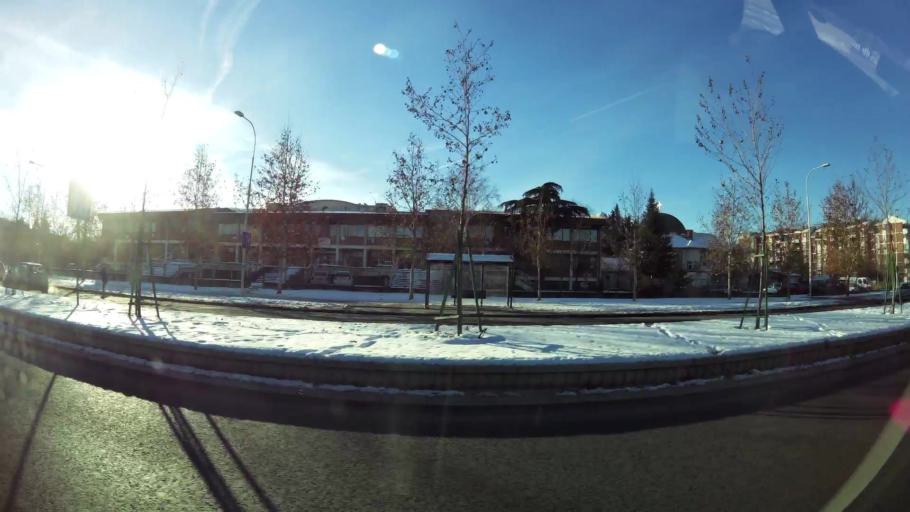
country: MK
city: Krushopek
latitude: 42.0102
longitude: 21.3624
